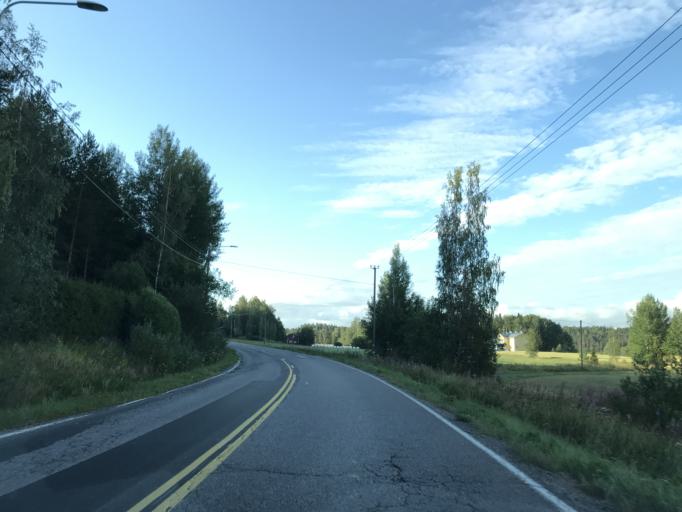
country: FI
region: Uusimaa
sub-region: Helsinki
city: Kauniainen
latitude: 60.3647
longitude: 24.6829
